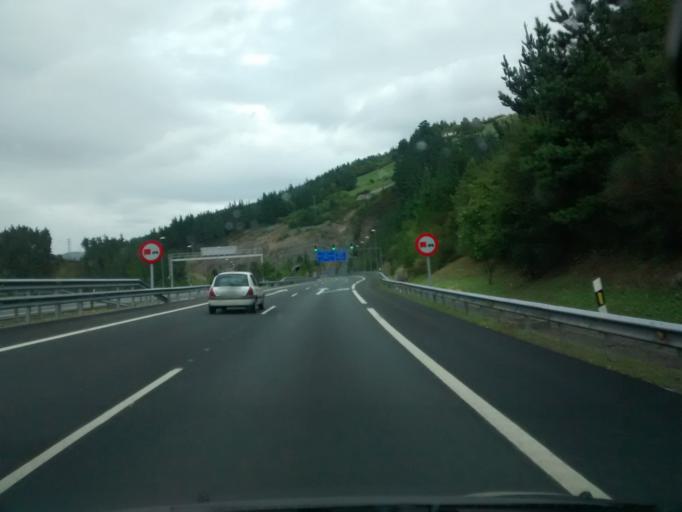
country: ES
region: Basque Country
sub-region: Provincia de Guipuzcoa
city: Bergara
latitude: 43.0823
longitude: -2.4429
